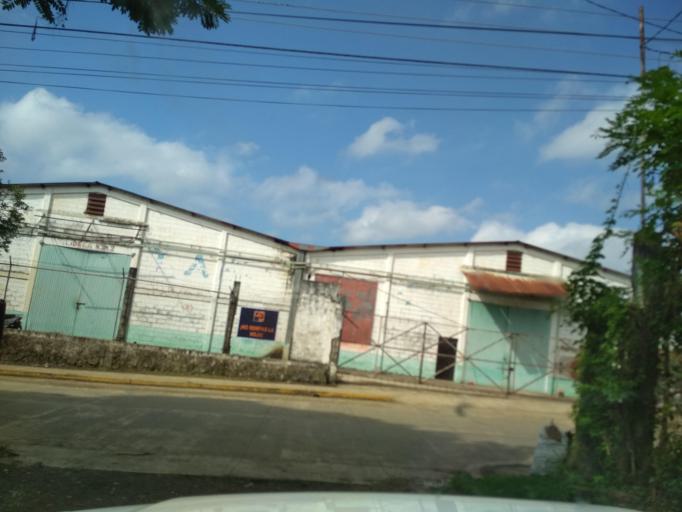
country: MX
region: Veracruz
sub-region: San Andres Tuxtla
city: Matacapan
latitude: 18.4401
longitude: -95.1769
